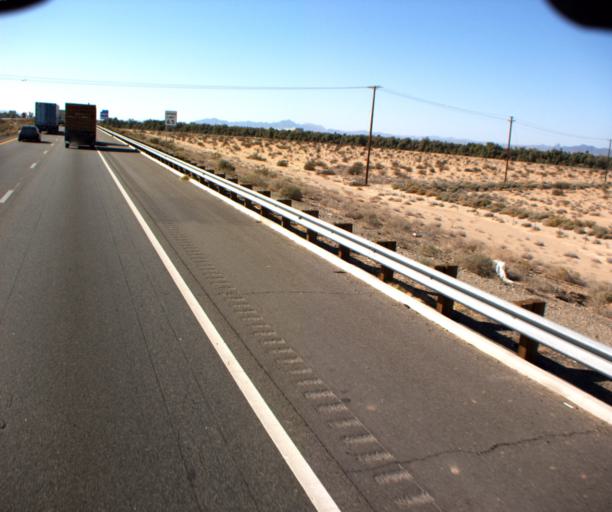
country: US
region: Arizona
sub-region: Yuma County
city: Fortuna Foothills
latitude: 32.6750
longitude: -114.4945
